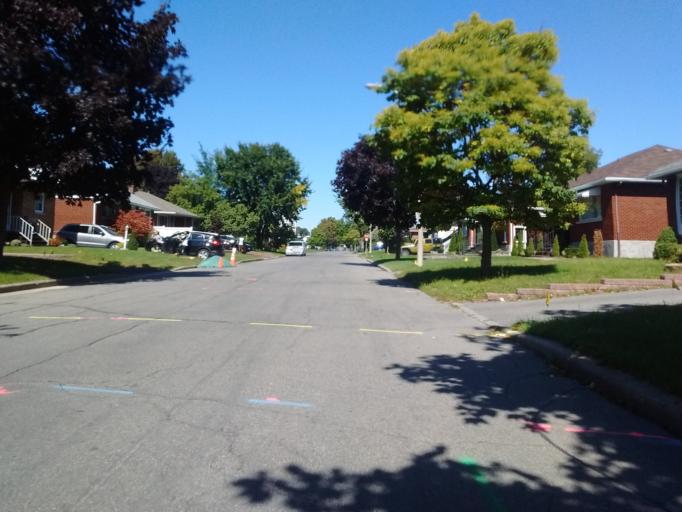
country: CA
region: Ontario
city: Ottawa
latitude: 45.4383
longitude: -75.6392
